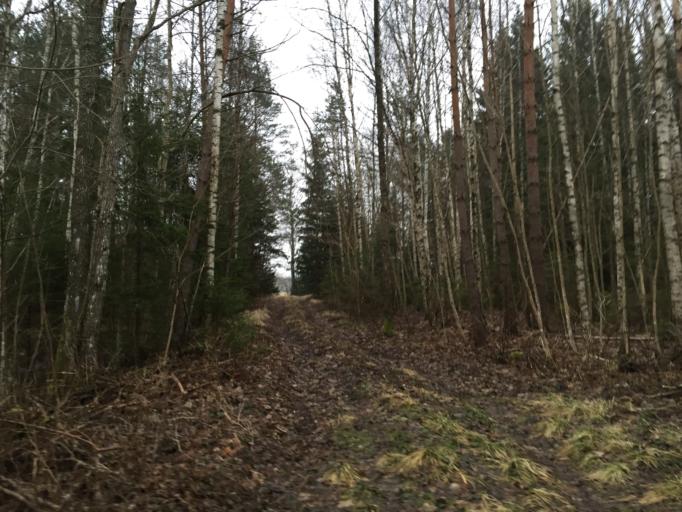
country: EE
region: Saare
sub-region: Kuressaare linn
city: Kuressaare
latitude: 58.4968
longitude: 22.3755
